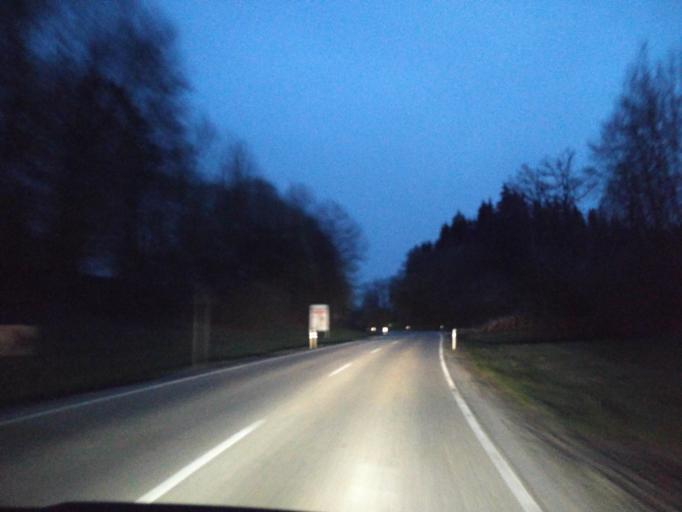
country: DE
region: Bavaria
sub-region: Upper Bavaria
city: Griesstatt
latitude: 47.9922
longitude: 12.1662
